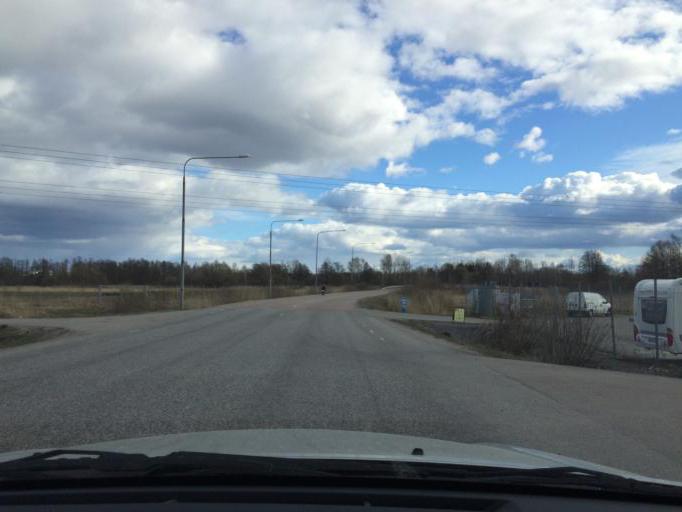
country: SE
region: Soedermanland
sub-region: Eskilstuna Kommun
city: Torshalla
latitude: 59.3865
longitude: 16.4679
